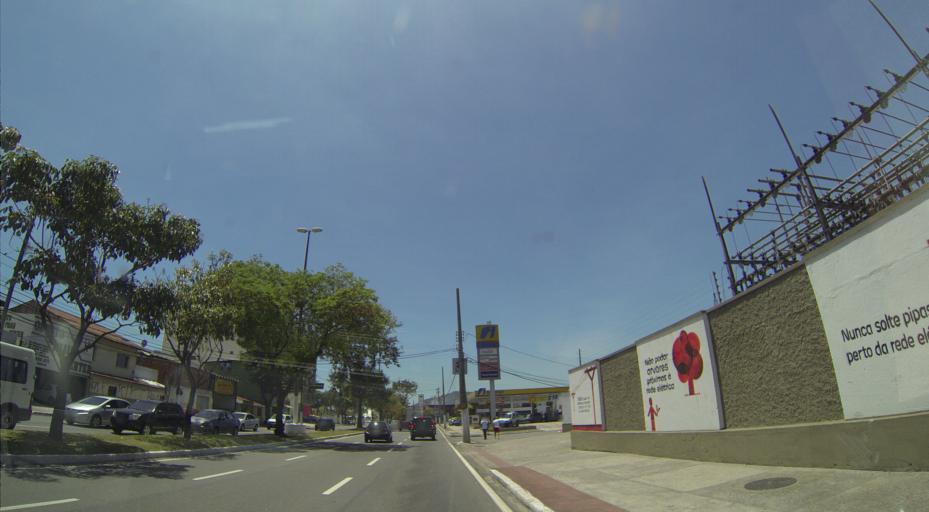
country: BR
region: Espirito Santo
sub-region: Vila Velha
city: Vila Velha
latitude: -20.3159
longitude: -40.3012
